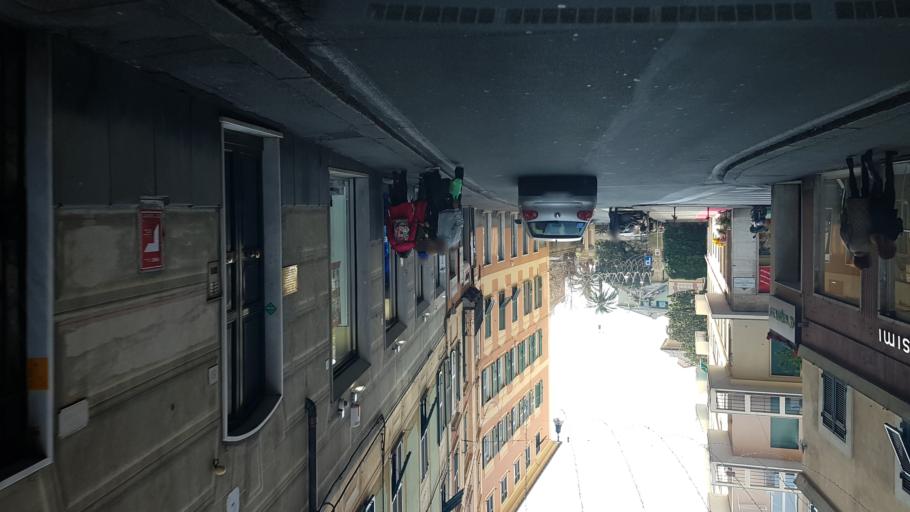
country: IT
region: Liguria
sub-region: Provincia di Genova
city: Bogliasco
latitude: 44.3841
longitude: 9.0363
